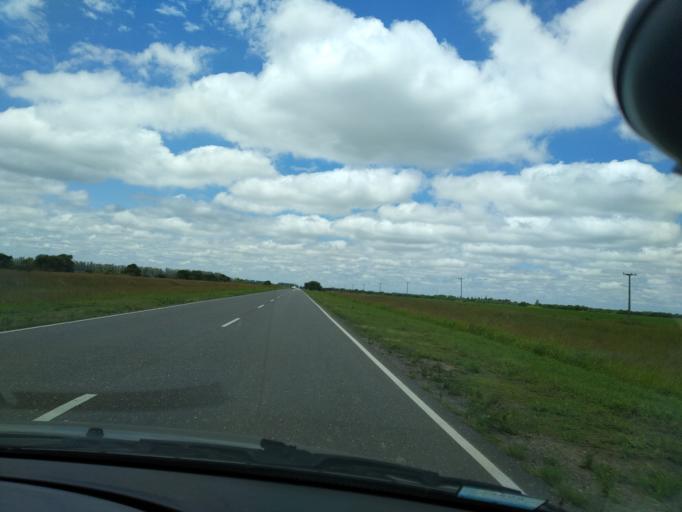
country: AR
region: Cordoba
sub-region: Departamento de Rio Segundo
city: Rio Segundo
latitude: -31.6434
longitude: -63.9653
